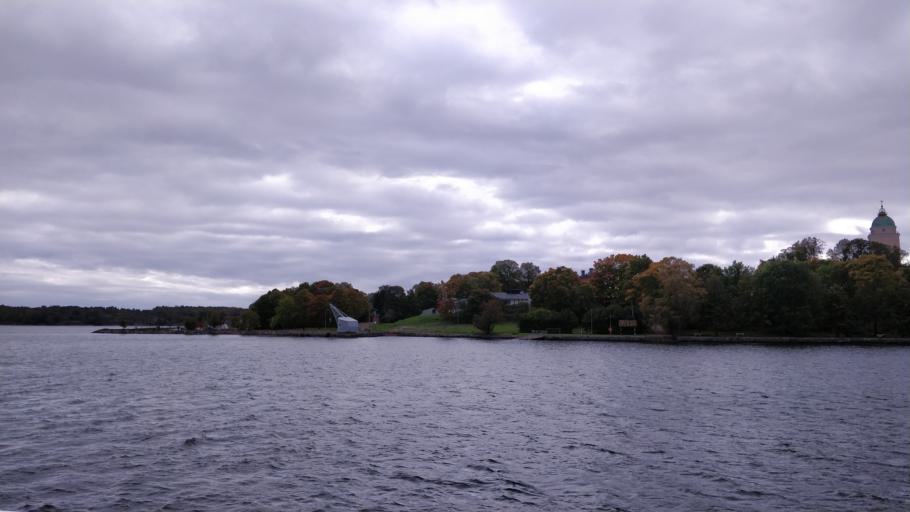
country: FI
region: Uusimaa
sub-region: Helsinki
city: Helsinki
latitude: 60.1508
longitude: 24.9898
